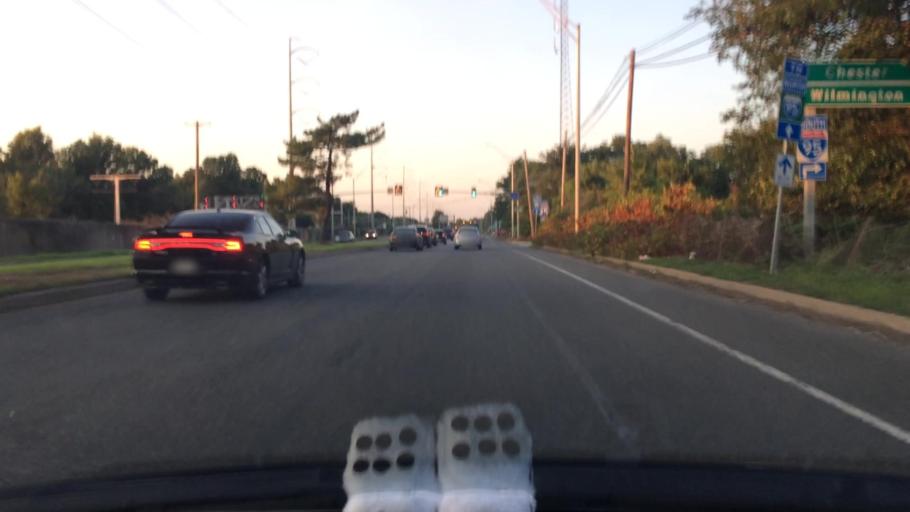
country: US
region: Pennsylvania
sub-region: Delaware County
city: Sharon Hill
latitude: 39.8808
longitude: -75.2541
